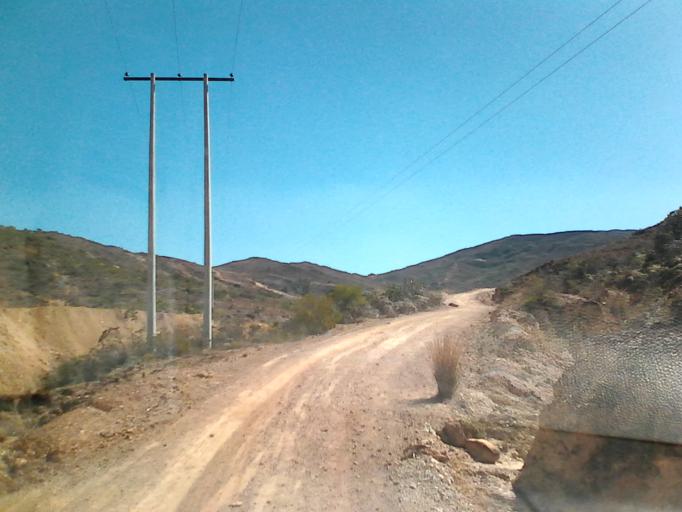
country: CO
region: Boyaca
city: Sachica
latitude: 5.5491
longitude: -73.5631
